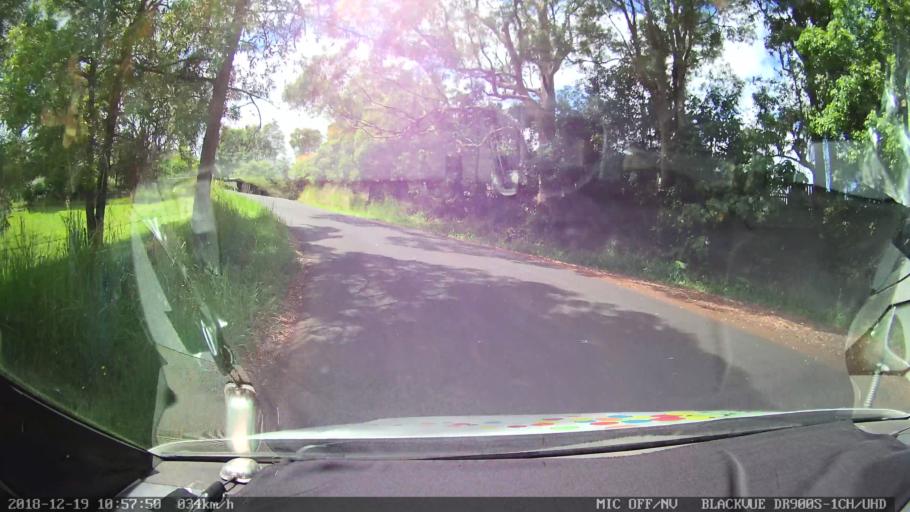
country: AU
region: New South Wales
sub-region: Lismore Municipality
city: Nimbin
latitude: -28.5911
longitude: 153.2620
